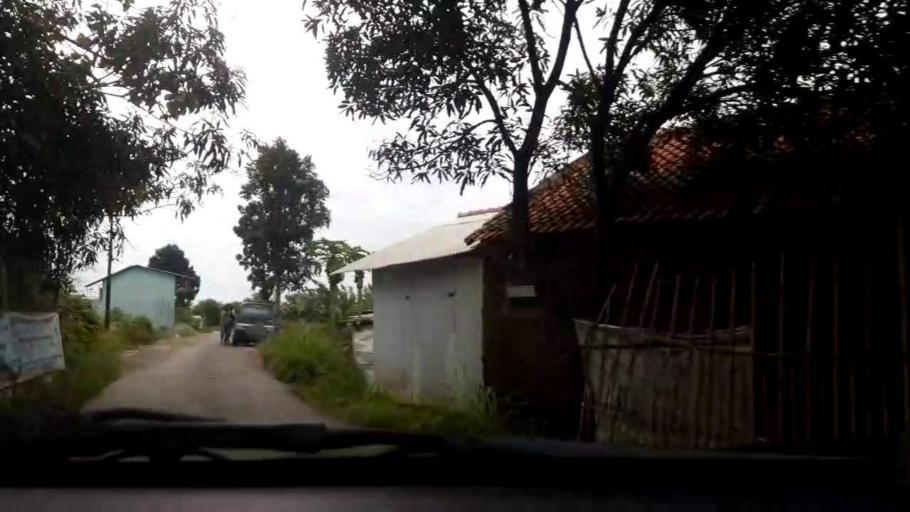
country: ID
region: West Java
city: Cileunyi
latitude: -6.9556
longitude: 107.7136
